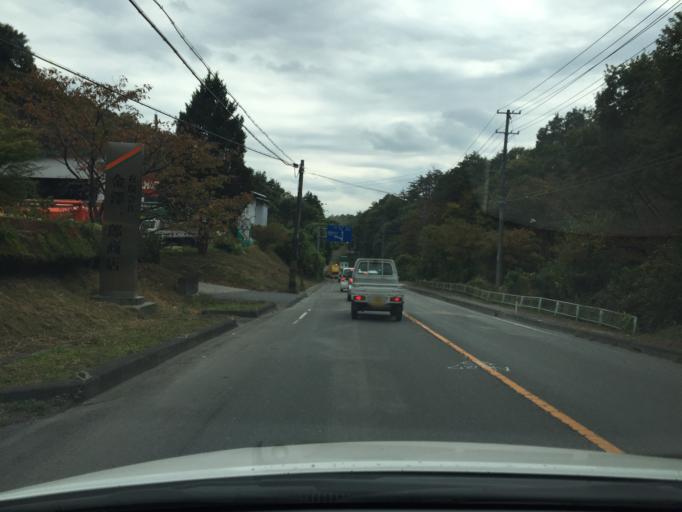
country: JP
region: Fukushima
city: Ishikawa
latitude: 37.0483
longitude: 140.3739
